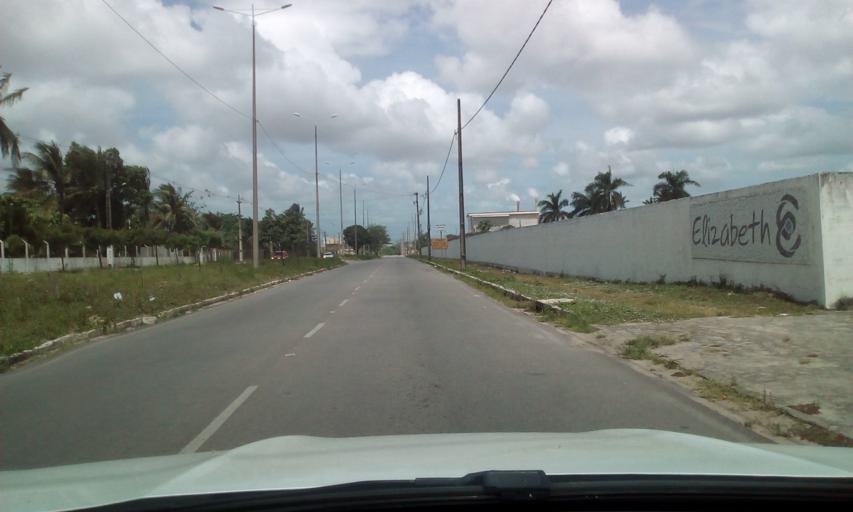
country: BR
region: Paraiba
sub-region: Bayeux
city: Bayeux
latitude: -7.1772
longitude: -34.9110
